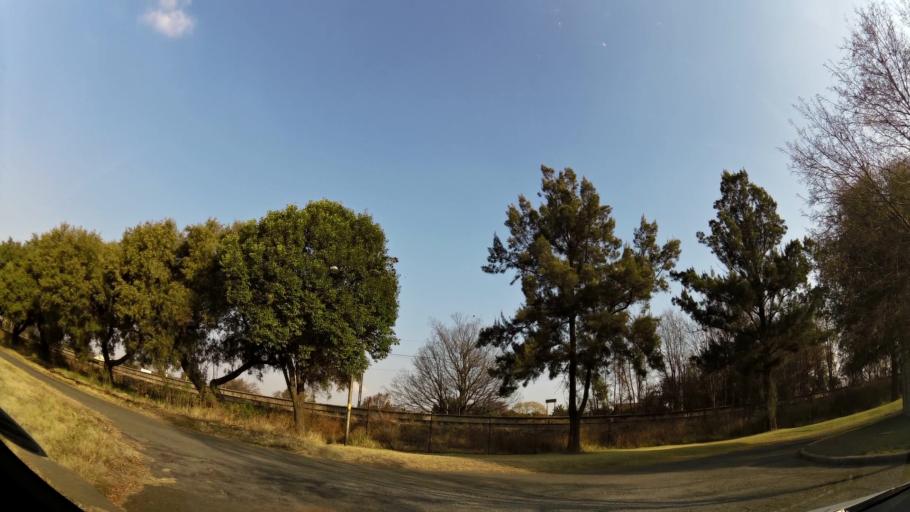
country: ZA
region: Gauteng
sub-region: Ekurhuleni Metropolitan Municipality
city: Springs
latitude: -26.2847
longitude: 28.4470
